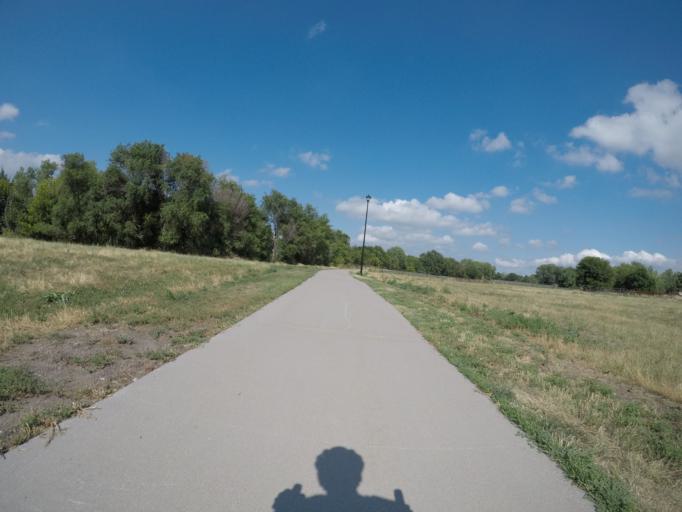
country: US
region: Nebraska
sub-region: Buffalo County
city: Kearney
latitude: 40.6744
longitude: -99.0547
